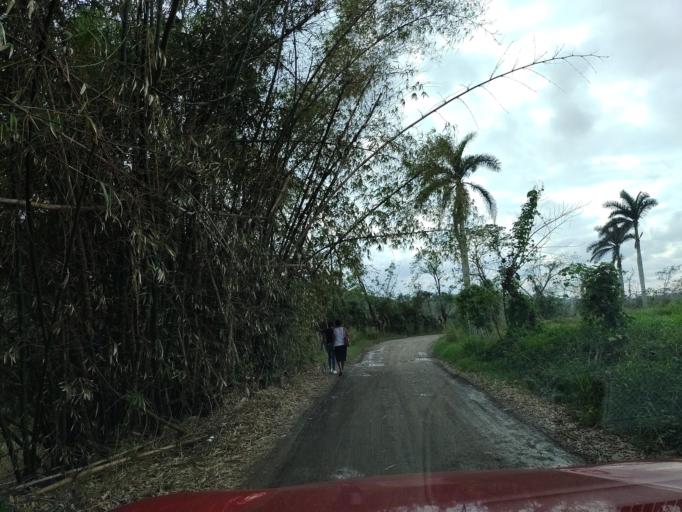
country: MX
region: Veracruz
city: Coatzintla
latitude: 20.4557
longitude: -97.4125
